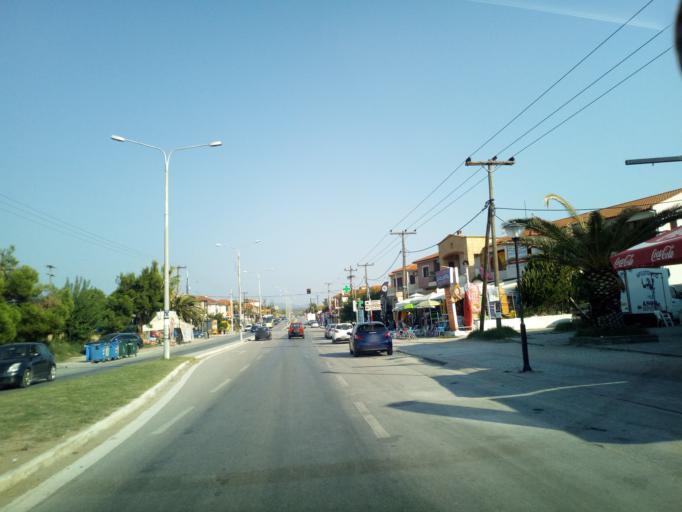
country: GR
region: Central Macedonia
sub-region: Nomos Chalkidikis
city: Nikiti
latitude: 40.2233
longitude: 23.6681
